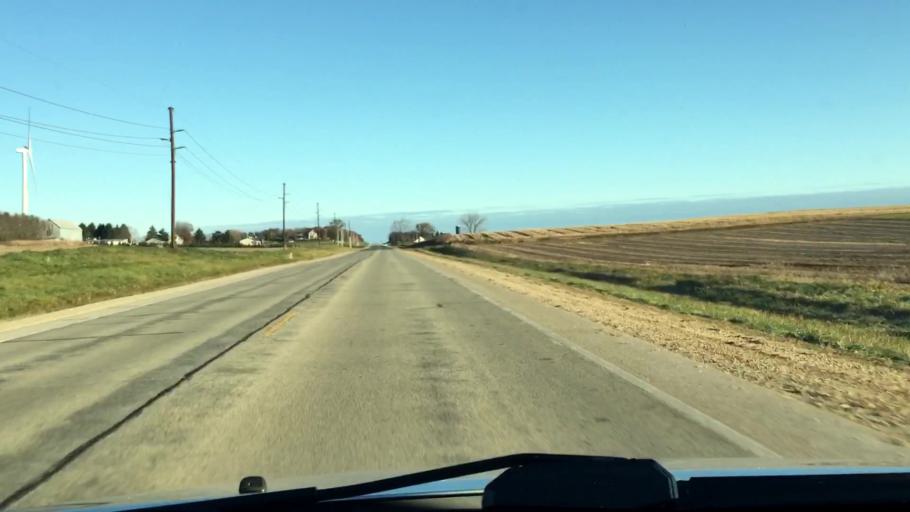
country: US
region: Wisconsin
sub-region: Washington County
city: Hartford
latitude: 43.3943
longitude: -88.4604
